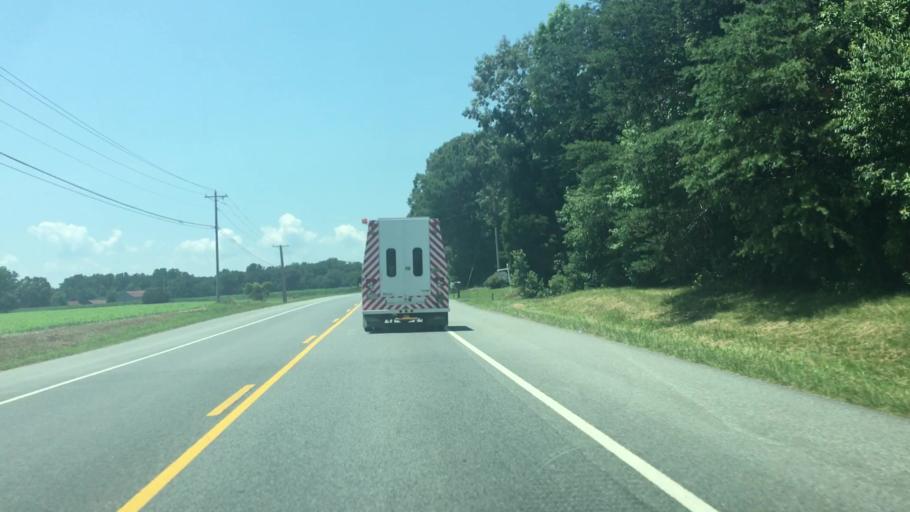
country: US
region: Maryland
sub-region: Saint Mary's County
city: Mechanicsville
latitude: 38.3724
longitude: -76.7981
